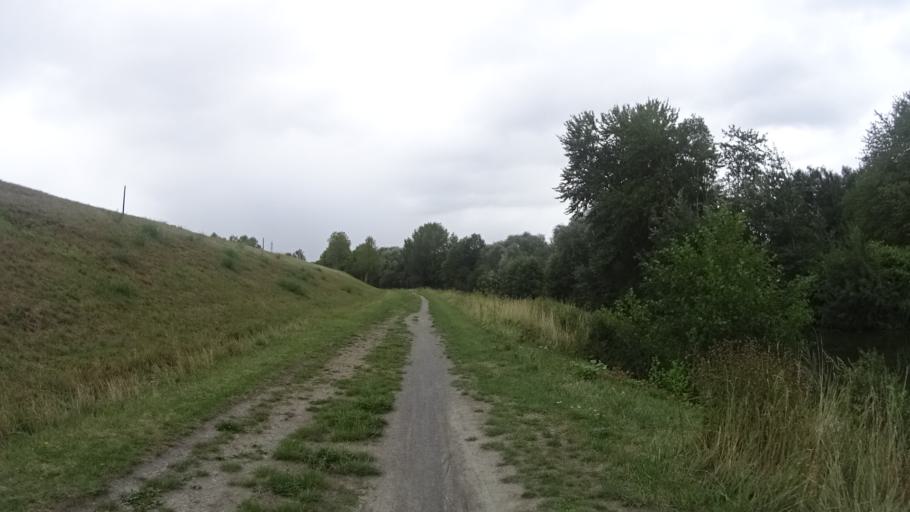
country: FR
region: Nord-Pas-de-Calais
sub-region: Departement du Nord
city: Hautmont
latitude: 50.2567
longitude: 3.9218
